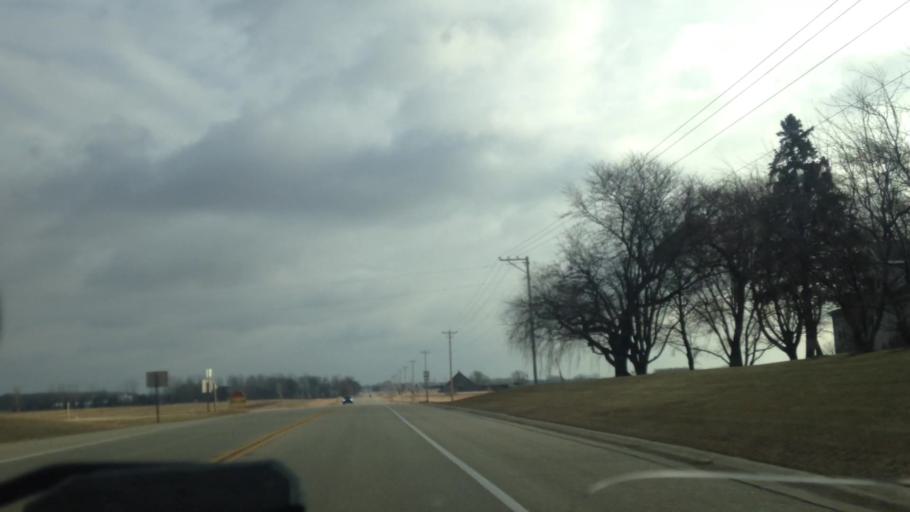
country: US
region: Wisconsin
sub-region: Dodge County
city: Juneau
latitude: 43.4450
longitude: -88.7430
